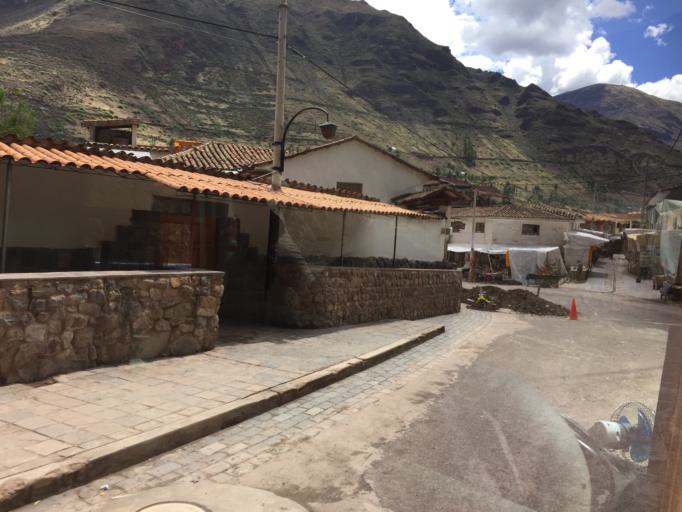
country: PE
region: Cusco
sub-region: Provincia de Calca
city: Pisac
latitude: -13.4204
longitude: -71.8479
